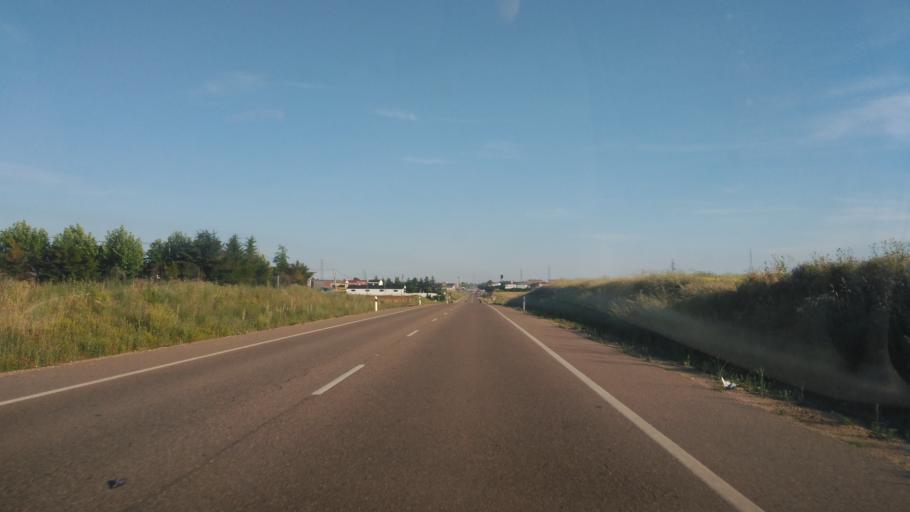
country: ES
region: Castille and Leon
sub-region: Provincia de Salamanca
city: Villares de la Reina
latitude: 41.0098
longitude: -5.6687
